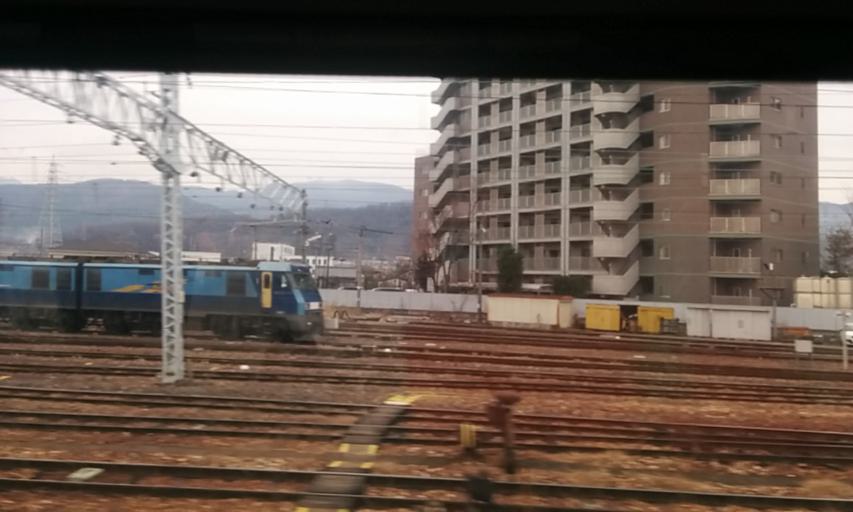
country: JP
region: Nagano
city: Matsumoto
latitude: 36.2084
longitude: 137.9688
